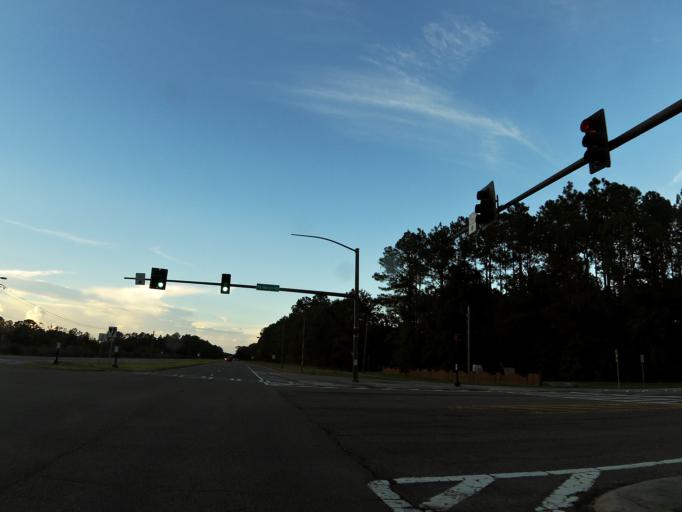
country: US
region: Georgia
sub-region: Camden County
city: Kings Bay Base
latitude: 30.7825
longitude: -81.5766
